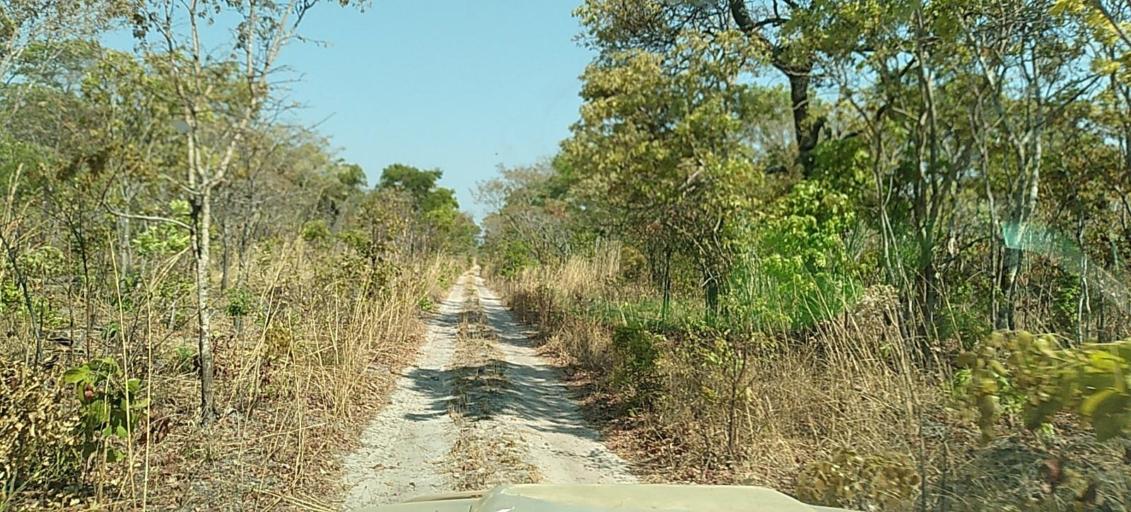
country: ZM
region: North-Western
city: Kalengwa
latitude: -13.3296
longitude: 24.8386
